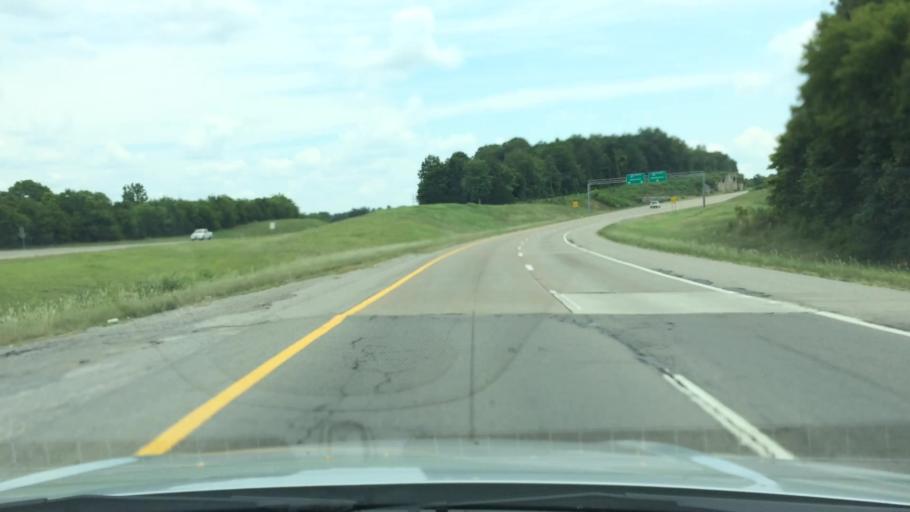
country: US
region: Tennessee
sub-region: Maury County
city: Spring Hill
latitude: 35.7389
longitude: -86.8813
